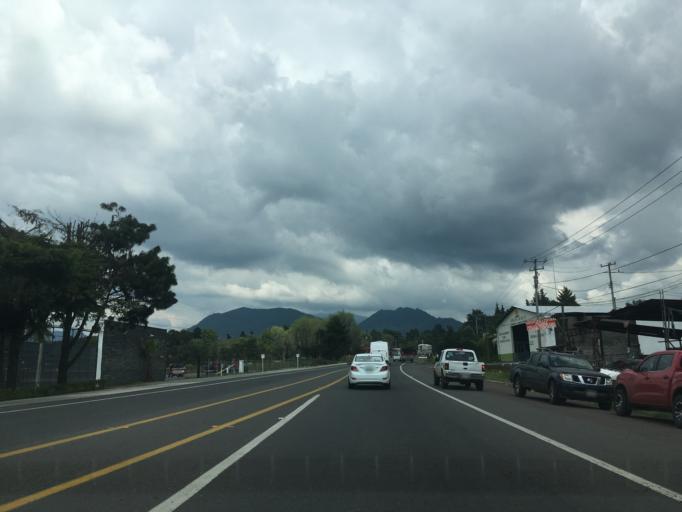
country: MX
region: Michoacan
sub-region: Uruapan
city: Uruapan
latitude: 19.4784
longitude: -102.0708
